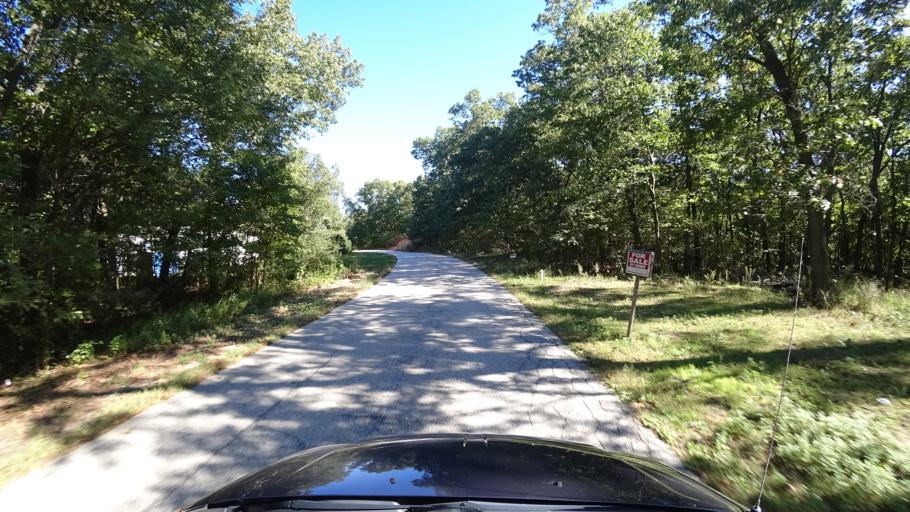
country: US
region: Indiana
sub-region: LaPorte County
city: Michigan City
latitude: 41.6955
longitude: -86.9265
